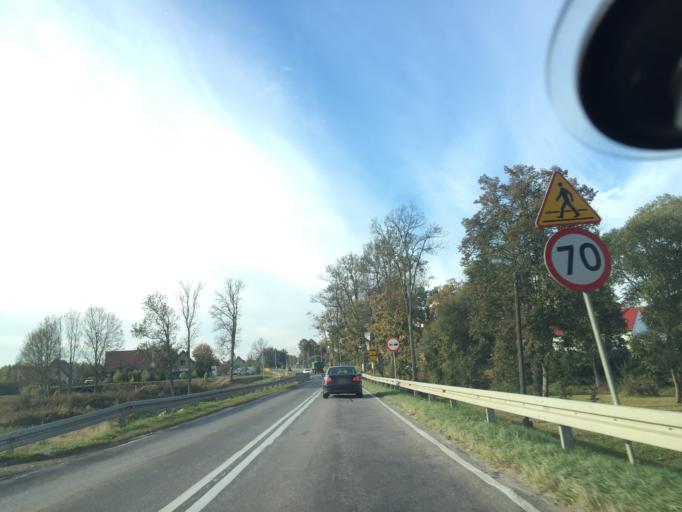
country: PL
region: Warmian-Masurian Voivodeship
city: Dobre Miasto
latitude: 54.0020
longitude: 20.4076
